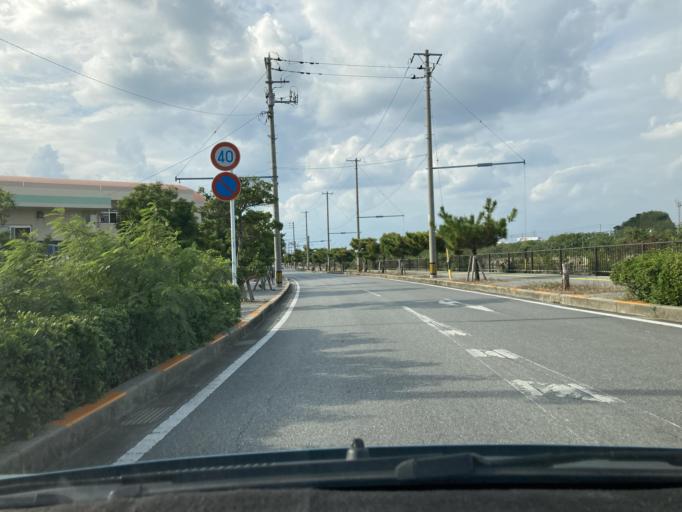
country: JP
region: Okinawa
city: Itoman
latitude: 26.1583
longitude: 127.6643
